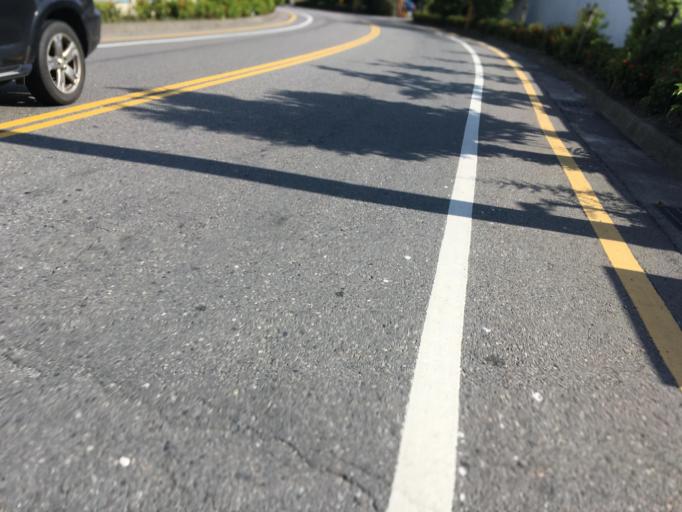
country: TW
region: Taiwan
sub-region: Yilan
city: Yilan
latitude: 24.6322
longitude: 121.8278
